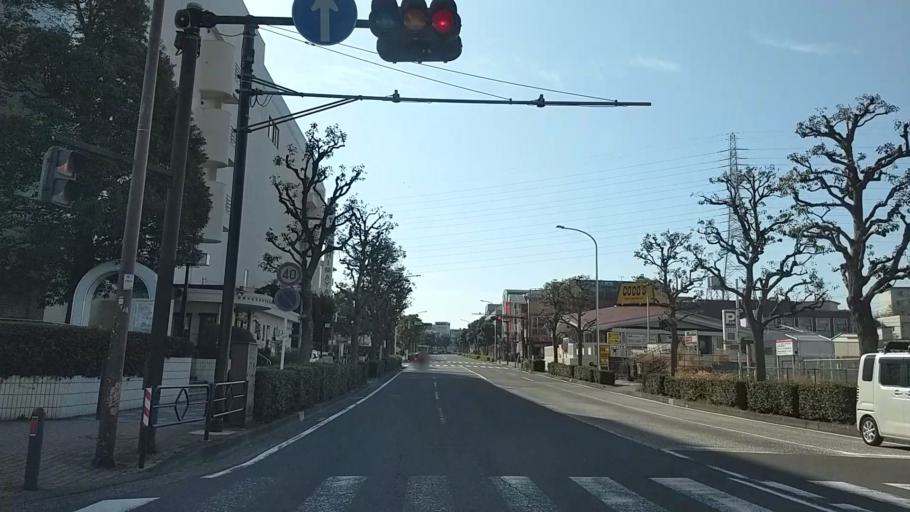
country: JP
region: Kanagawa
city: Kamakura
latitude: 35.3746
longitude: 139.5765
